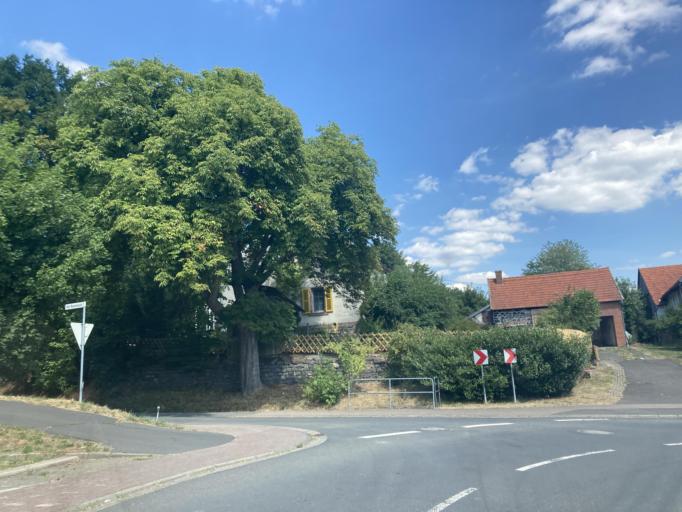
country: DE
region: Hesse
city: Grebenau
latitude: 50.7230
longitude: 9.4194
